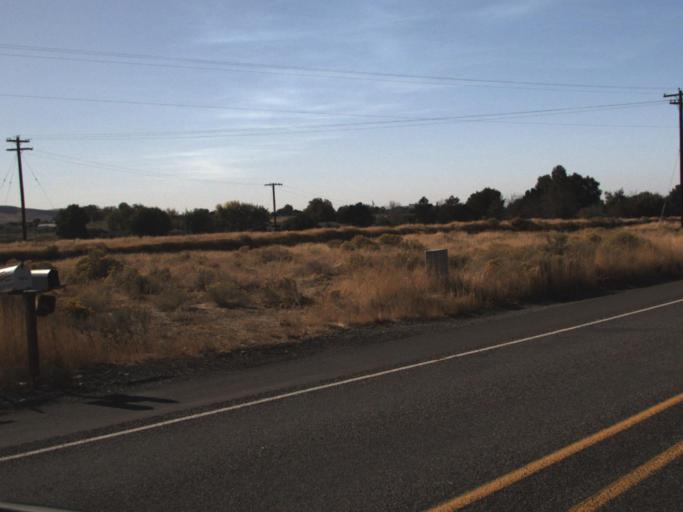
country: US
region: Washington
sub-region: Benton County
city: Finley
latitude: 46.1841
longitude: -119.0709
